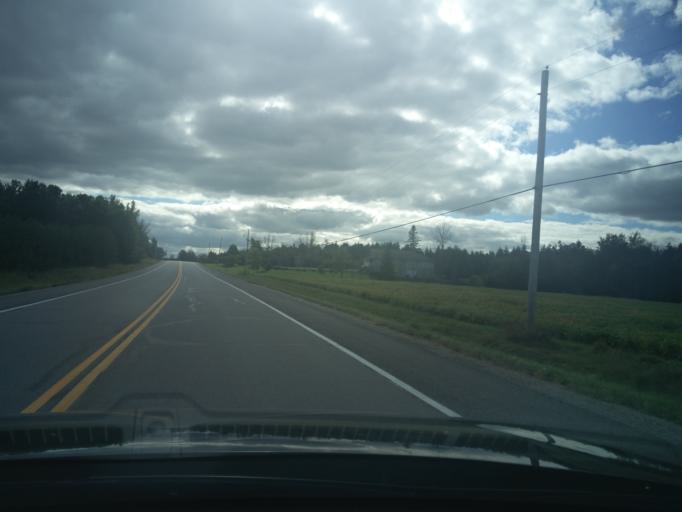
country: CA
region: Ontario
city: Perth
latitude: 44.9730
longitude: -76.1397
